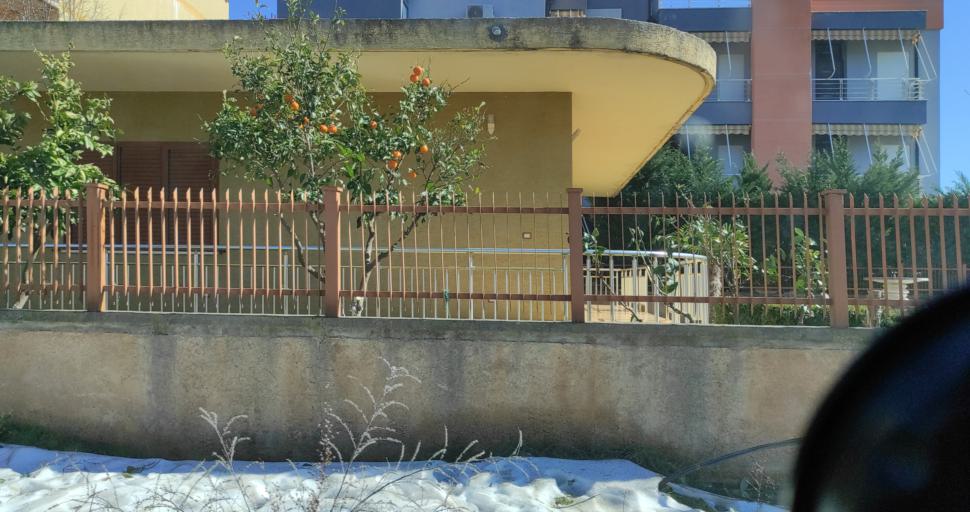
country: AL
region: Shkoder
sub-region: Rrethi i Shkodres
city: Velipoje
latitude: 41.8655
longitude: 19.4105
